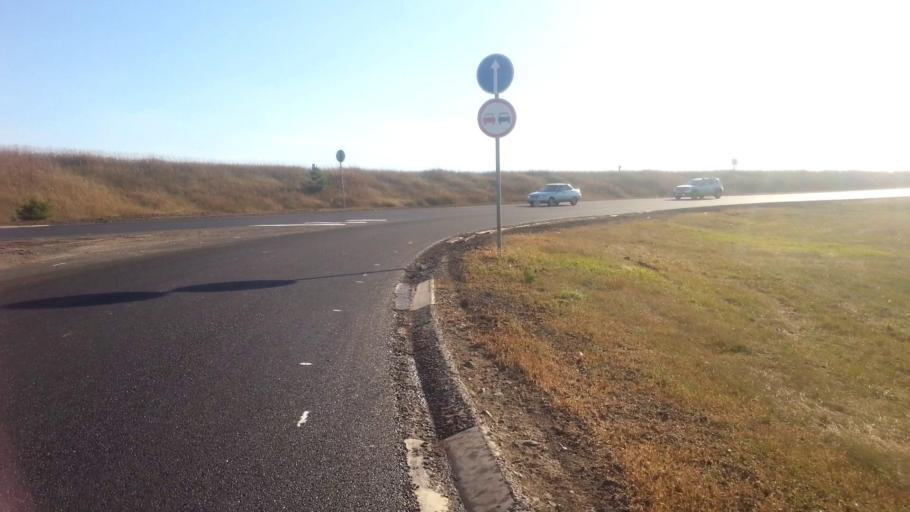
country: RU
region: Altai Krai
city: Novoaltaysk
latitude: 53.3704
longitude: 83.9570
